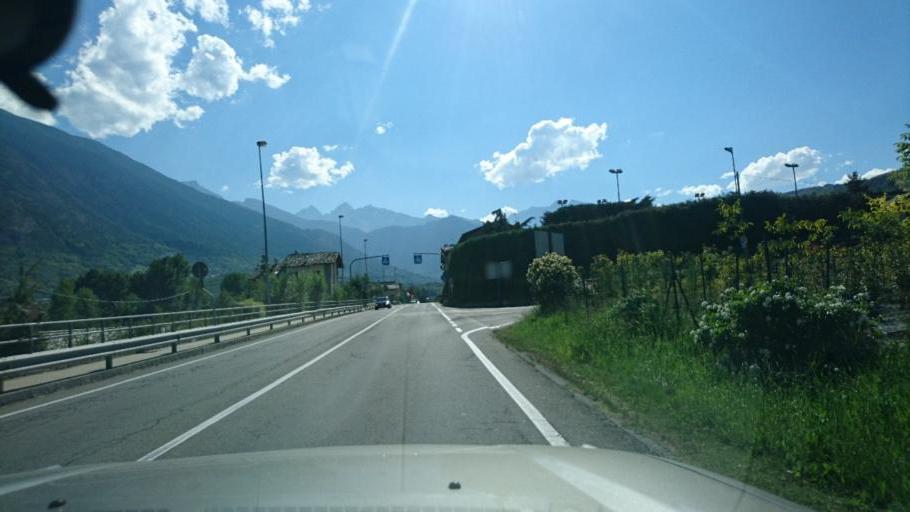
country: IT
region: Aosta Valley
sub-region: Valle d'Aosta
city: Saint Maurice
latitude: 45.7188
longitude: 7.2629
